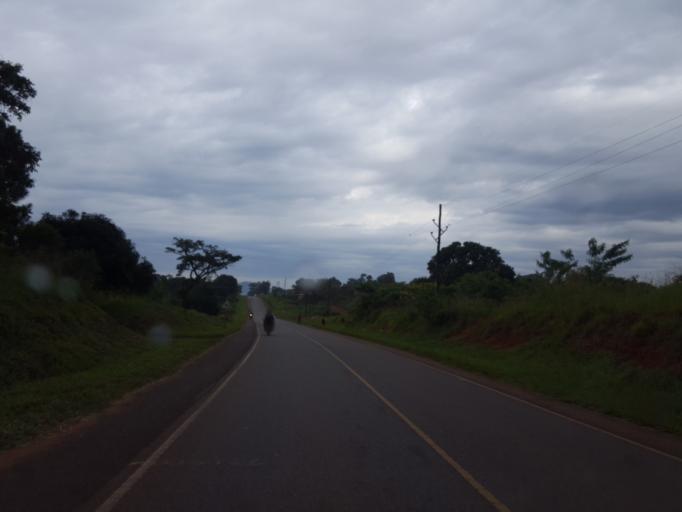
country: UG
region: Central Region
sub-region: Kiboga District
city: Kiboga
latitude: 0.9604
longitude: 31.7417
